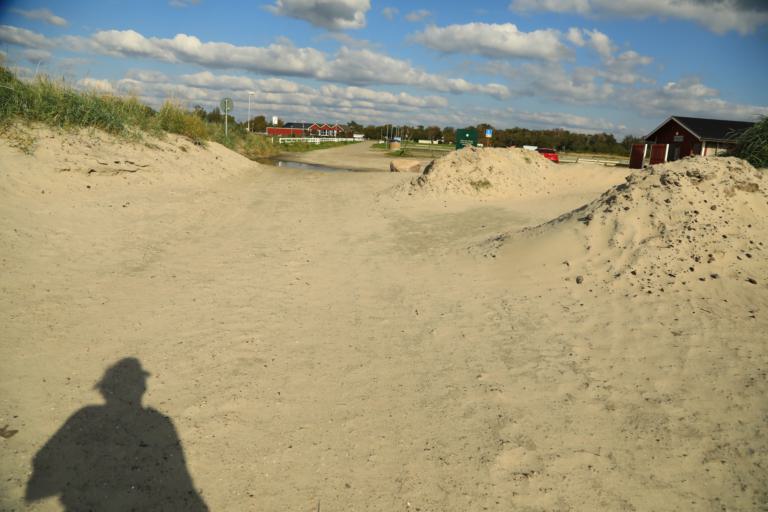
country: SE
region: Halland
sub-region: Varbergs Kommun
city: Tvaaker
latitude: 57.0078
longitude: 12.3483
